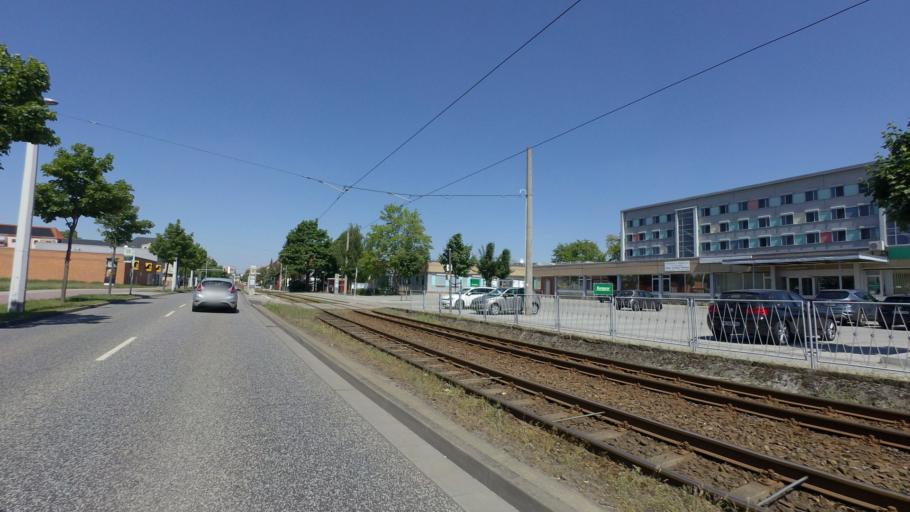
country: DE
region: Brandenburg
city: Cottbus
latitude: 51.7400
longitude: 14.3344
